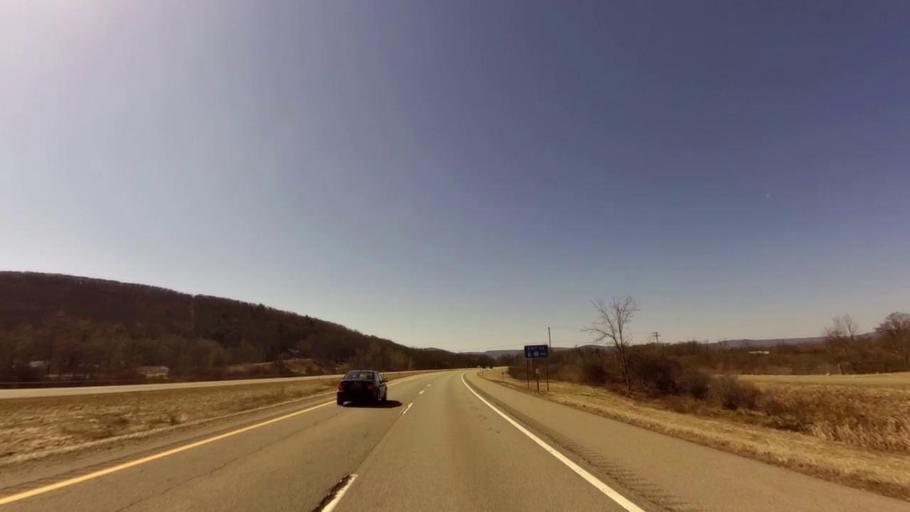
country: US
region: New York
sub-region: Cattaraugus County
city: Franklinville
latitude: 42.3110
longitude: -78.4602
